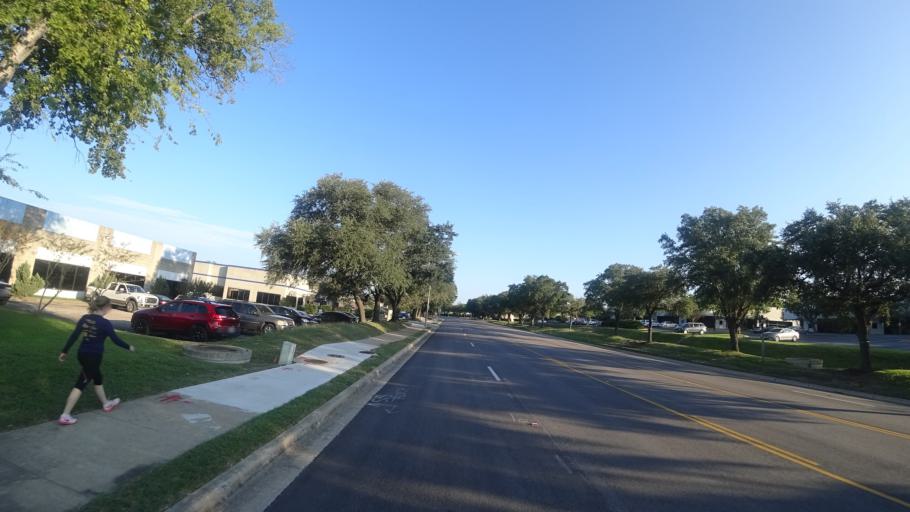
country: US
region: Texas
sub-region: Travis County
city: Austin
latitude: 30.3399
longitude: -97.6768
